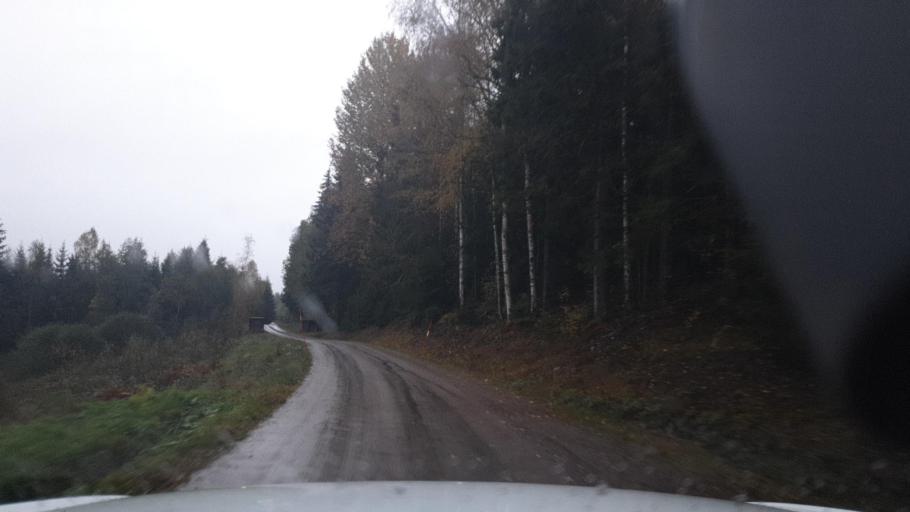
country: SE
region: Vaermland
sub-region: Eda Kommun
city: Amotfors
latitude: 59.7969
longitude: 12.4253
